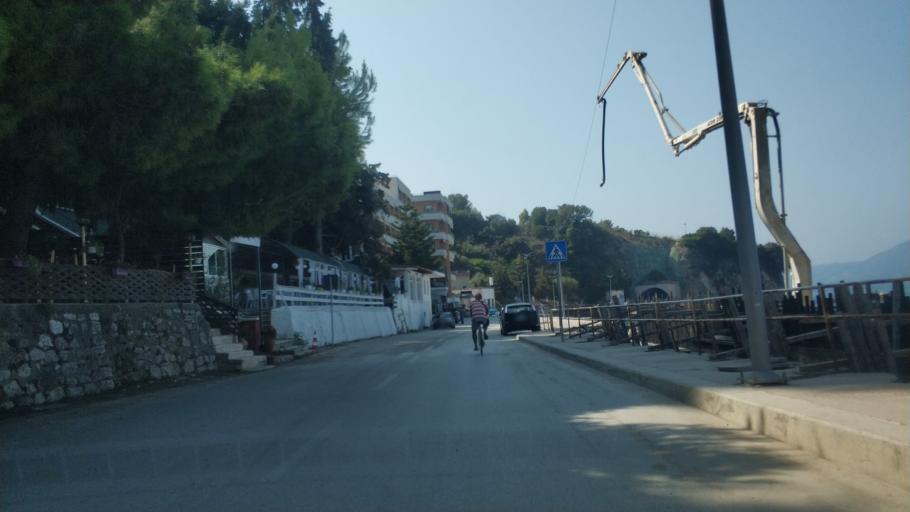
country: AL
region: Vlore
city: Vlore
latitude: 40.4230
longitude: 19.4894
